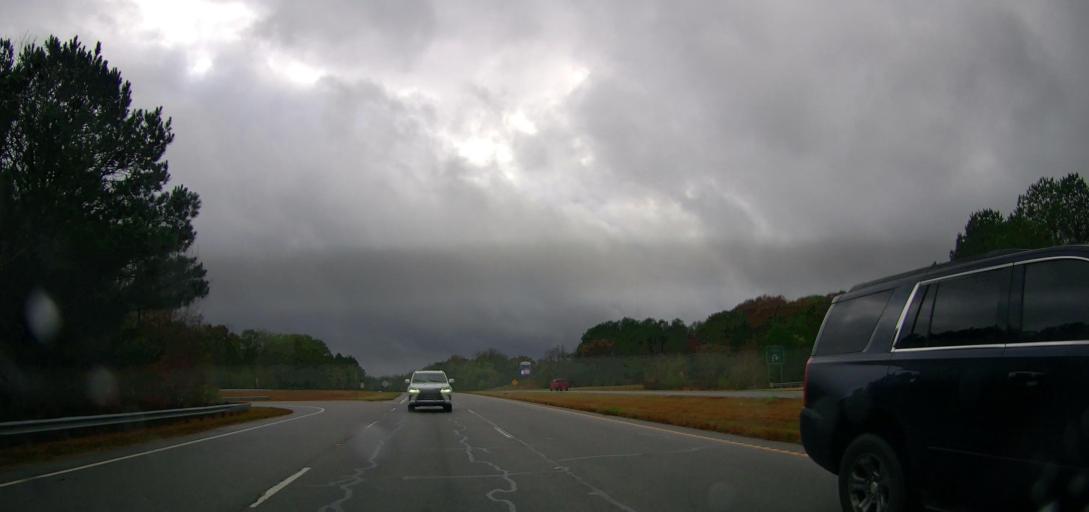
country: US
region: Georgia
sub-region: Oconee County
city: Watkinsville
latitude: 33.8685
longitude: -83.4229
